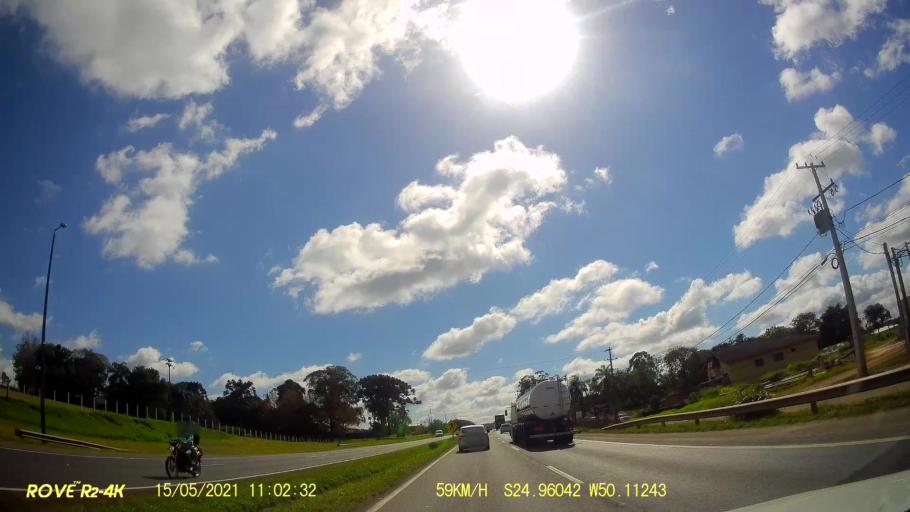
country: BR
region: Parana
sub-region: Carambei
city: Carambei
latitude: -24.9605
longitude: -50.1125
